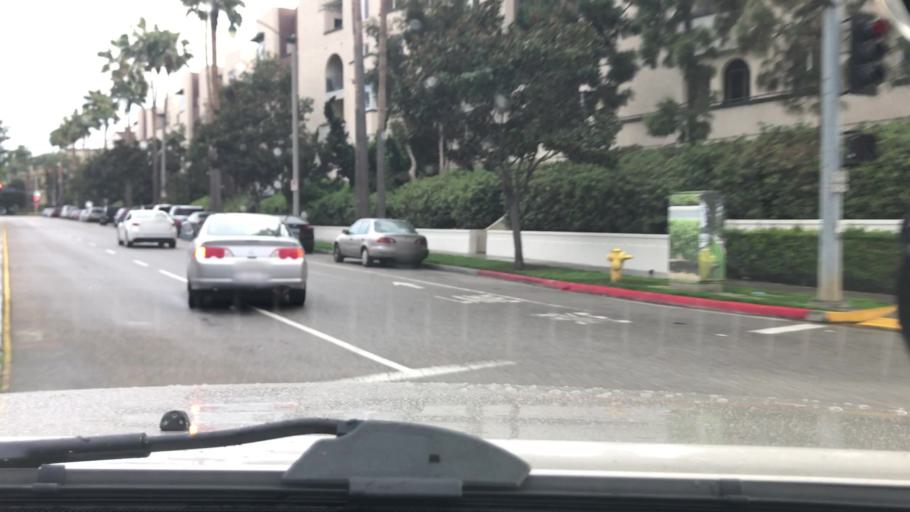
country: US
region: California
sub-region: Los Angeles County
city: Marina del Rey
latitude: 33.9731
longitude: -118.4276
